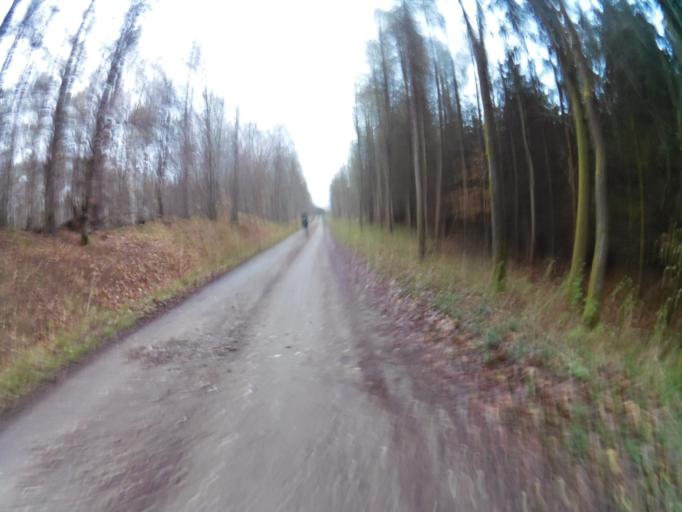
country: PL
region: West Pomeranian Voivodeship
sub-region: Powiat szczecinecki
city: Borne Sulinowo
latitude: 53.6570
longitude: 16.5205
